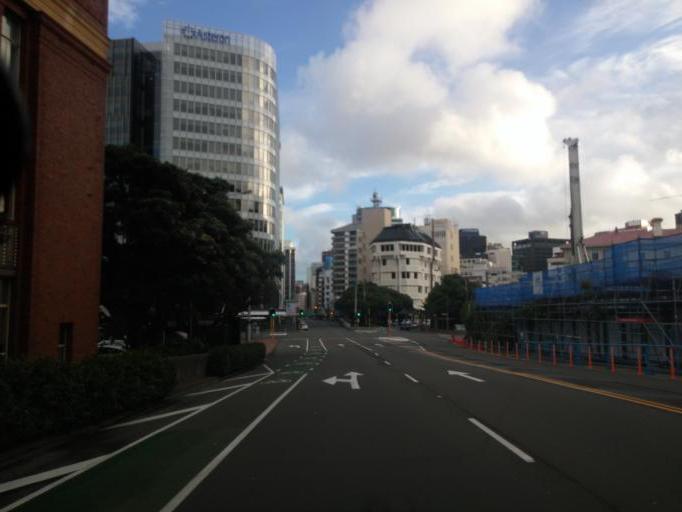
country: NZ
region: Wellington
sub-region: Wellington City
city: Wellington
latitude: -41.2789
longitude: 174.7797
